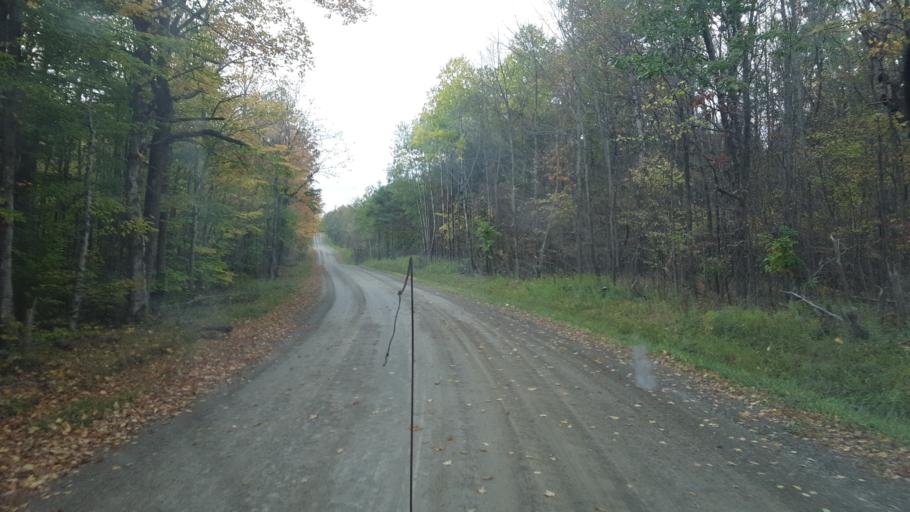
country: US
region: New York
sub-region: Allegany County
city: Alfred
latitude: 42.3908
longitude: -77.8690
